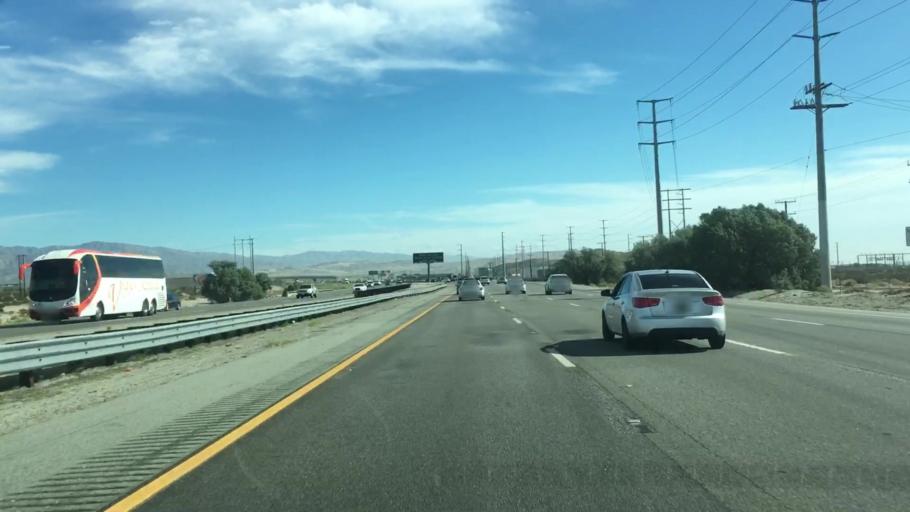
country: US
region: California
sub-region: Riverside County
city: Garnet
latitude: 33.9056
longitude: -116.5611
